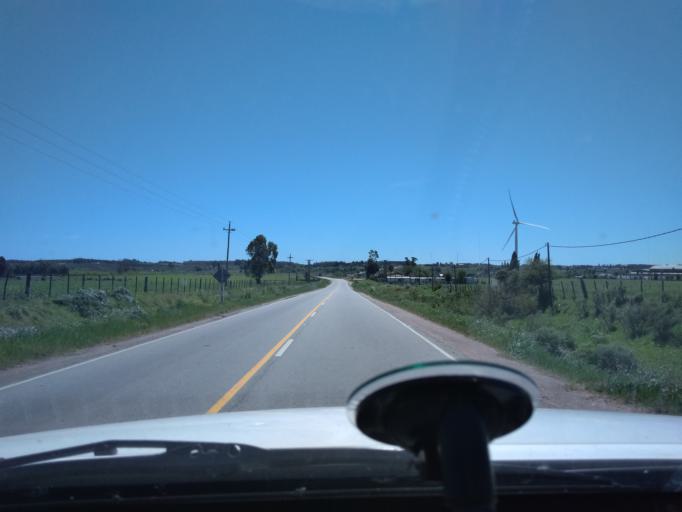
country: UY
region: Canelones
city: Progreso
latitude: -34.6942
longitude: -56.2966
